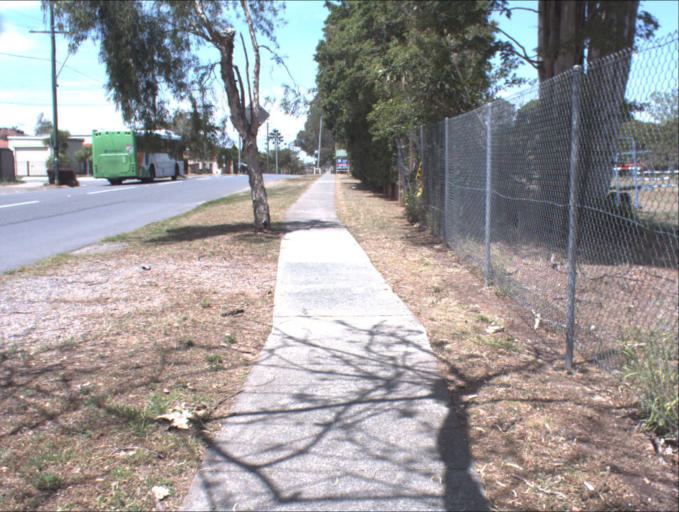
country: AU
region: Queensland
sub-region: Logan
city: Rochedale South
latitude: -27.5893
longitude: 153.1230
